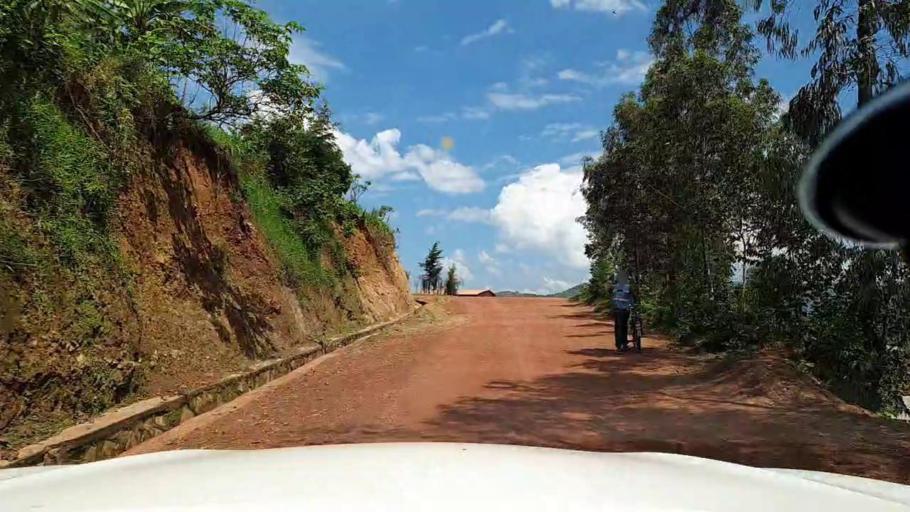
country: RW
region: Northern Province
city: Byumba
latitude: -1.7377
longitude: 29.8622
